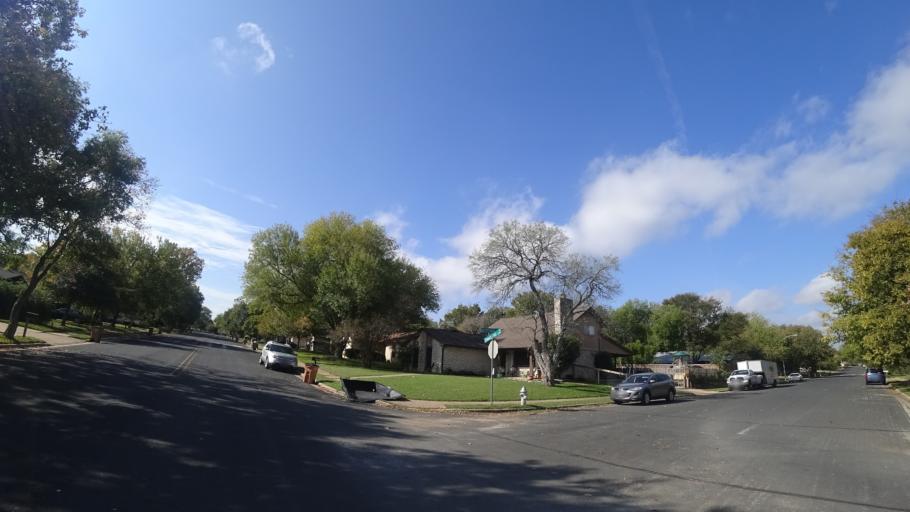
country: US
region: Texas
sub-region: Travis County
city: Shady Hollow
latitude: 30.1948
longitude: -97.8220
